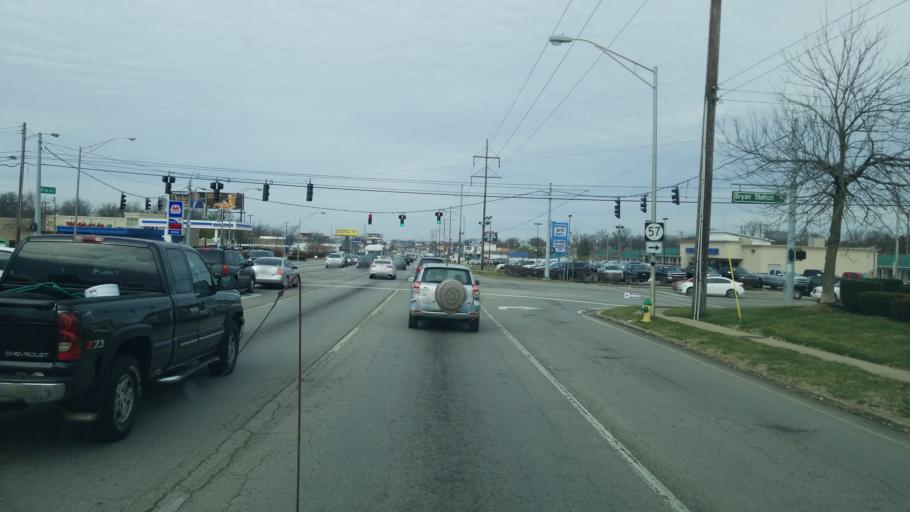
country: US
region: Kentucky
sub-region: Fayette County
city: Lexington-Fayette
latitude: 38.0597
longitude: -84.4644
